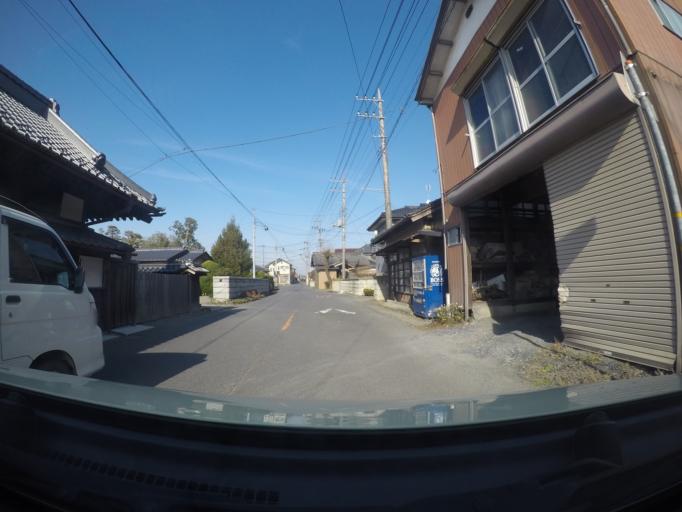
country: JP
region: Ibaraki
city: Tsukuba
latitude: 36.2233
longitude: 140.0660
